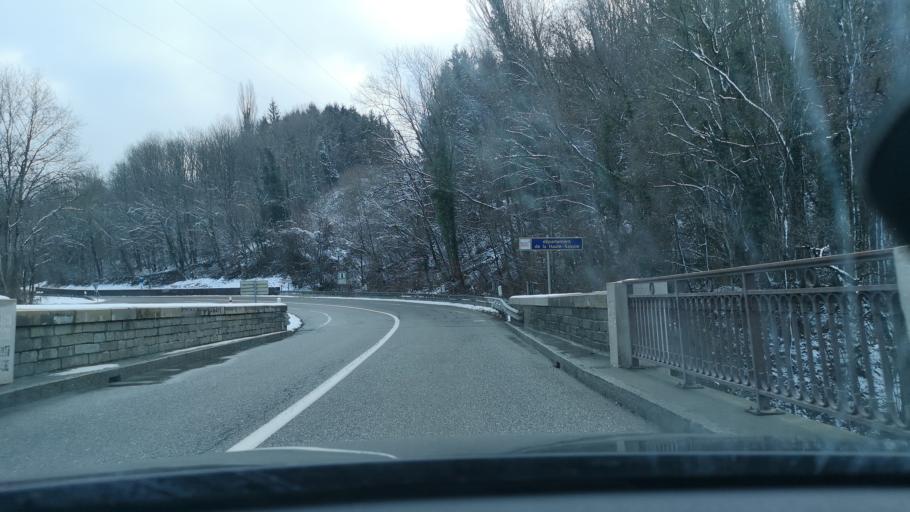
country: FR
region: Rhone-Alpes
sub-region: Departement de l'Ain
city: Collonges
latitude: 46.1203
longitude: 5.9046
